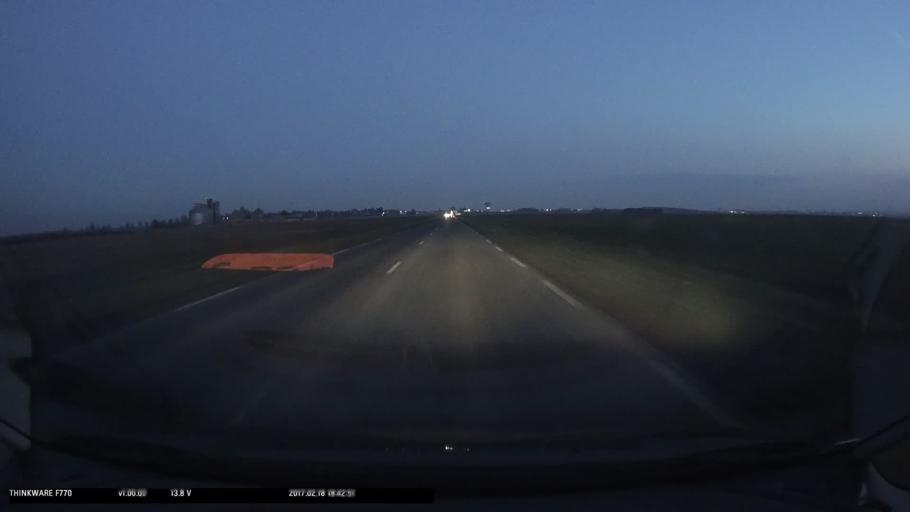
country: FR
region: Ile-de-France
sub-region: Departement du Val-d'Oise
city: Osny
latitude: 49.0962
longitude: 2.0495
